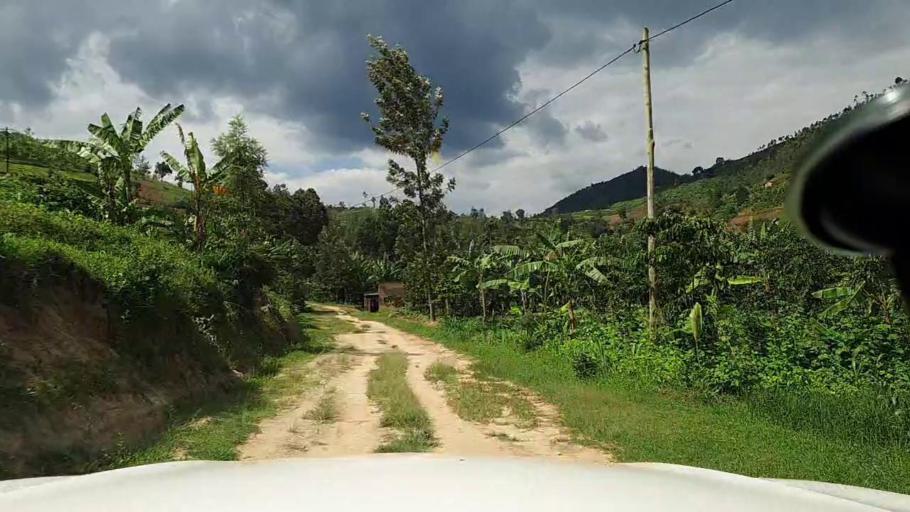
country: RW
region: Southern Province
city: Gitarama
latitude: -1.8255
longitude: 29.8019
